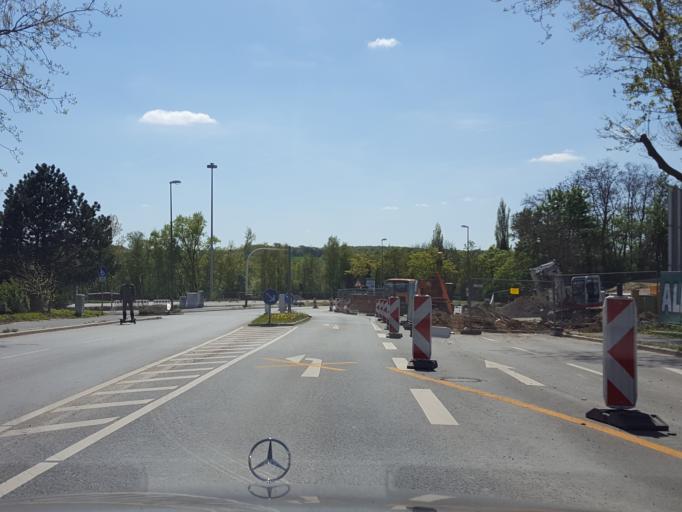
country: DE
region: North Rhine-Westphalia
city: Witten
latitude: 51.4820
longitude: 7.3258
